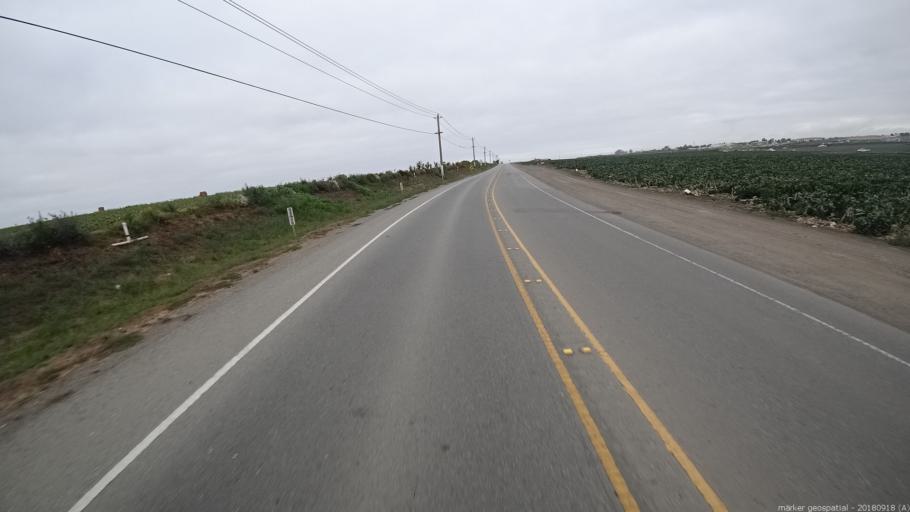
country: US
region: California
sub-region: Monterey County
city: Castroville
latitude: 36.7428
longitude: -121.7343
